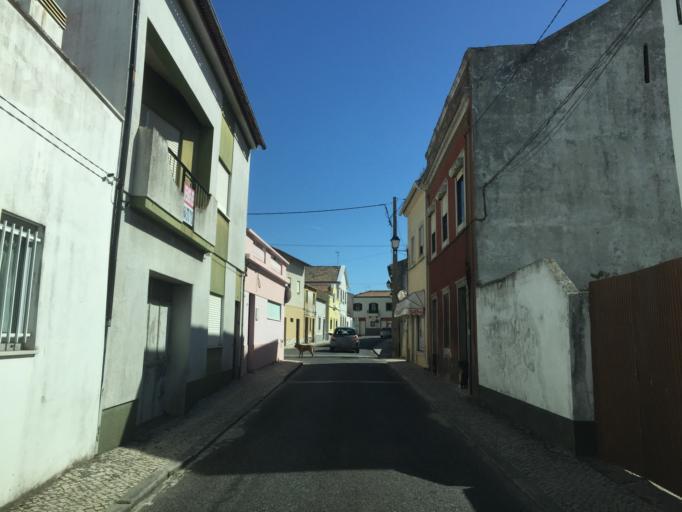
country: PT
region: Coimbra
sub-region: Figueira da Foz
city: Tavarede
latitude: 40.2138
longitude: -8.8513
